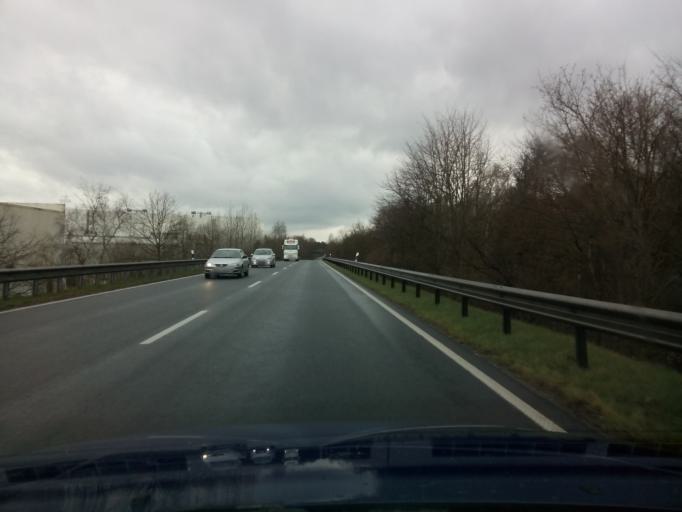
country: DE
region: Lower Saxony
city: Herzlake
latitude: 52.6941
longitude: 7.6052
